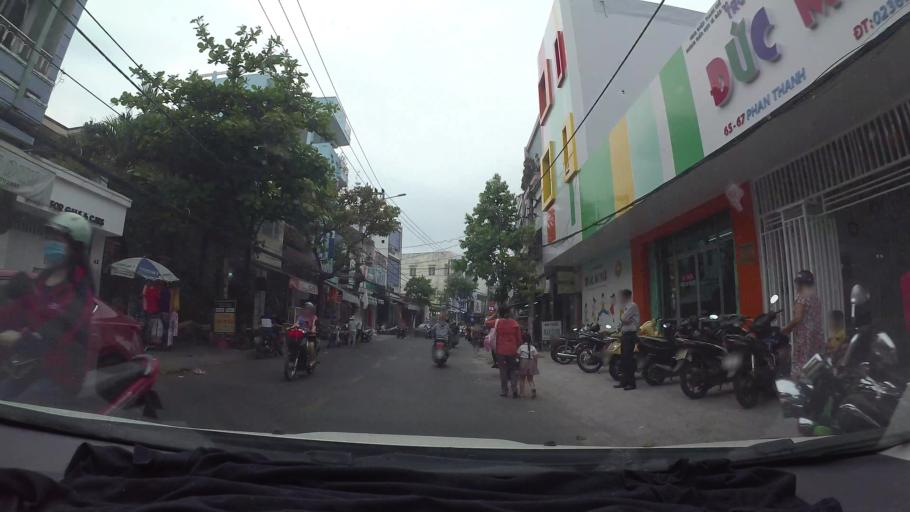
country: VN
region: Da Nang
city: Da Nang
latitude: 16.0641
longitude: 108.2082
